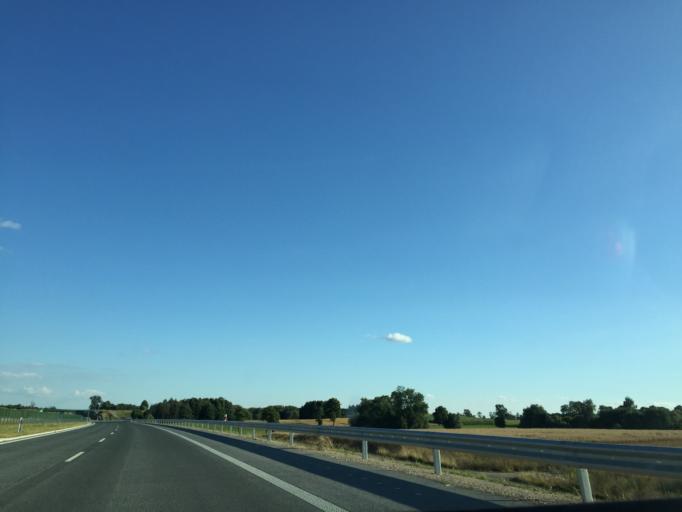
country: PL
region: Podlasie
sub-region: Powiat grajewski
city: Szczuczyn
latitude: 53.5580
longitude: 22.2608
